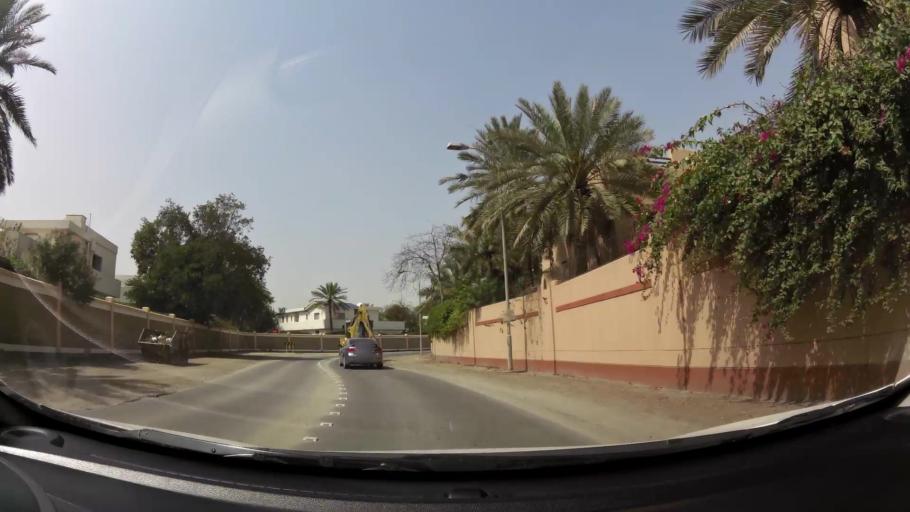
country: BH
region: Manama
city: Jidd Hafs
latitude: 26.2247
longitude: 50.4964
